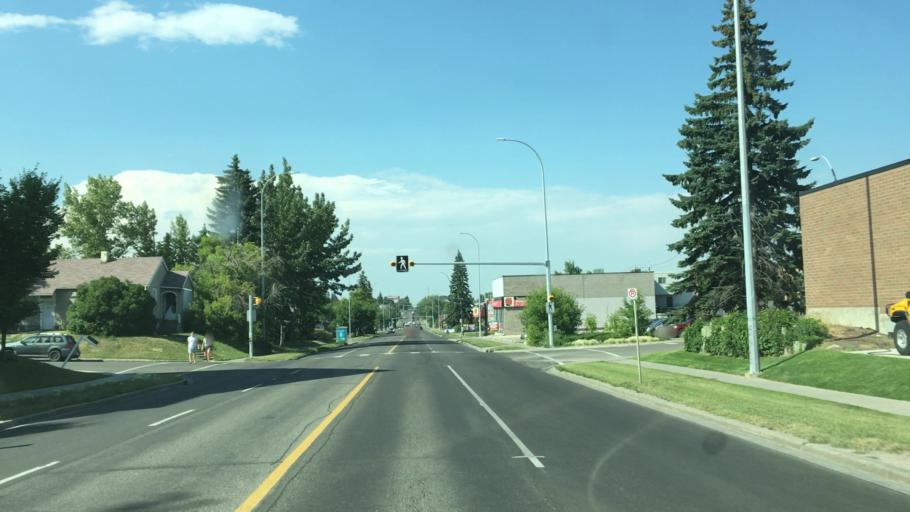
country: CA
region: Alberta
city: Calgary
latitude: 51.0738
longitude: -114.0625
